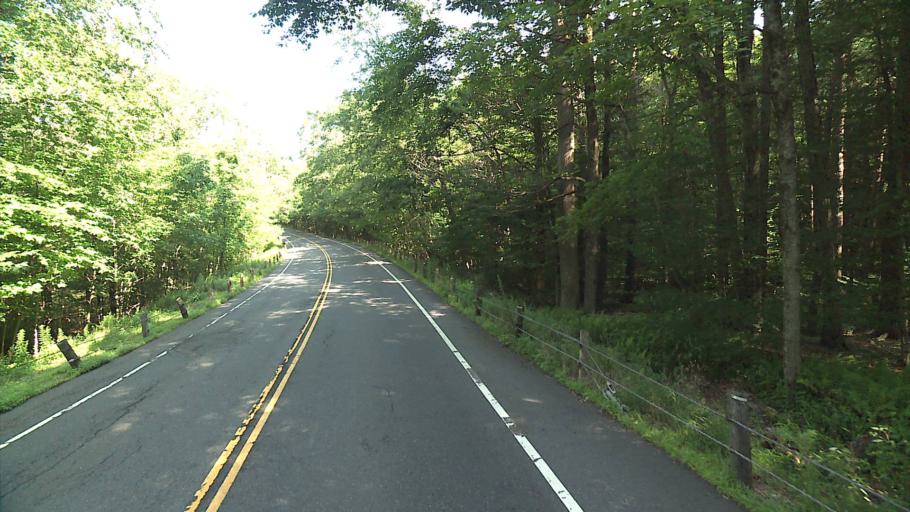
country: US
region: Massachusetts
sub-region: Hampden County
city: Granville
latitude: 42.0260
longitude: -72.9556
